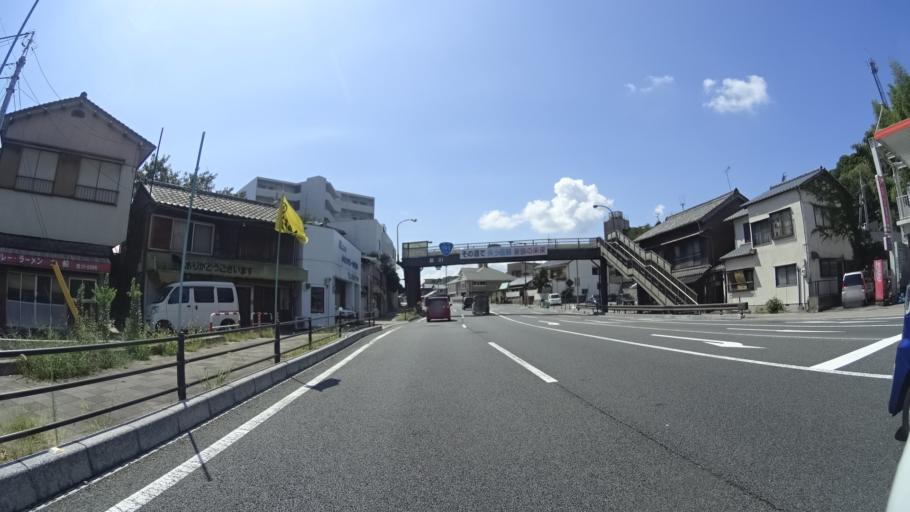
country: JP
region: Yamaguchi
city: Shimonoseki
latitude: 33.9653
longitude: 130.9185
